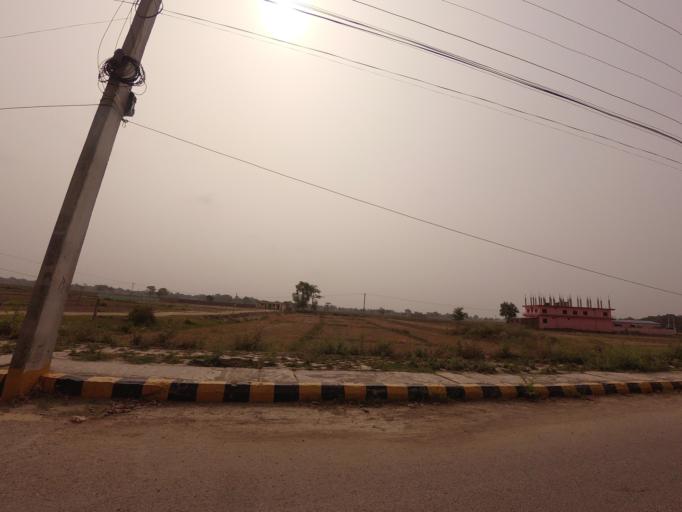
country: IN
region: Uttar Pradesh
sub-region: Maharajganj
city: Nautanwa
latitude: 27.4634
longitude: 83.2837
